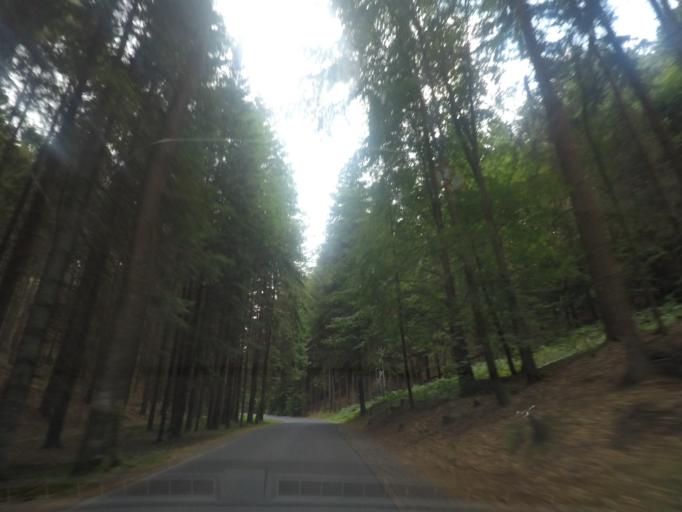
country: CZ
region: Ustecky
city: Ceska Kamenice
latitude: 50.8505
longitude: 14.4108
